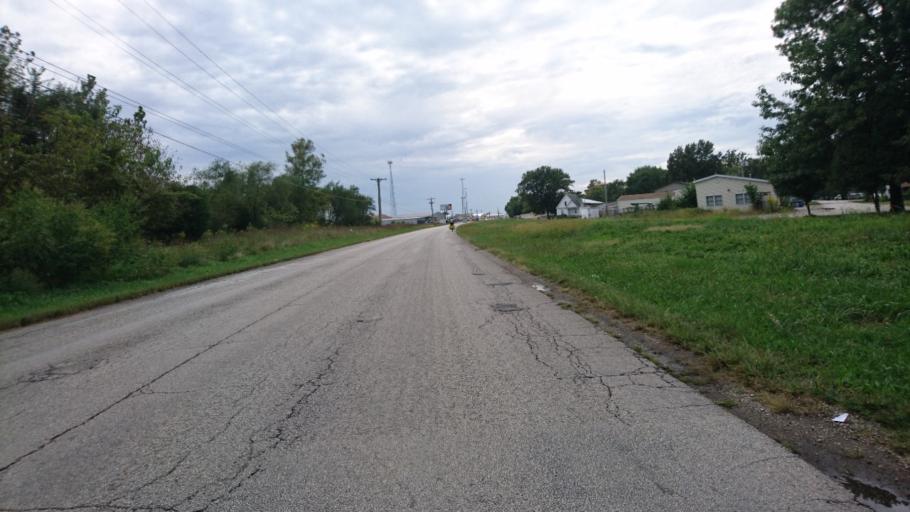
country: US
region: Illinois
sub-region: Sangamon County
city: Southern View
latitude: 39.7694
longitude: -89.6560
